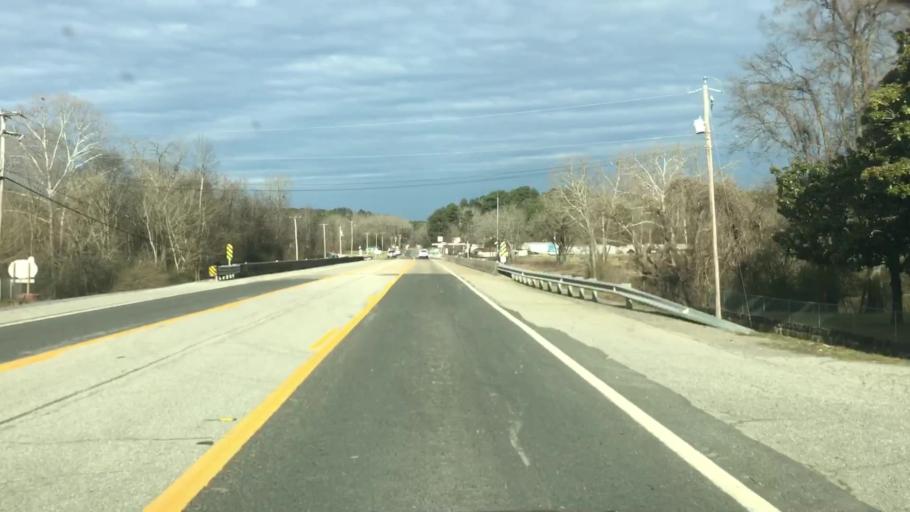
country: US
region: Arkansas
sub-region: Montgomery County
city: Mount Ida
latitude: 34.5599
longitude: -93.6353
